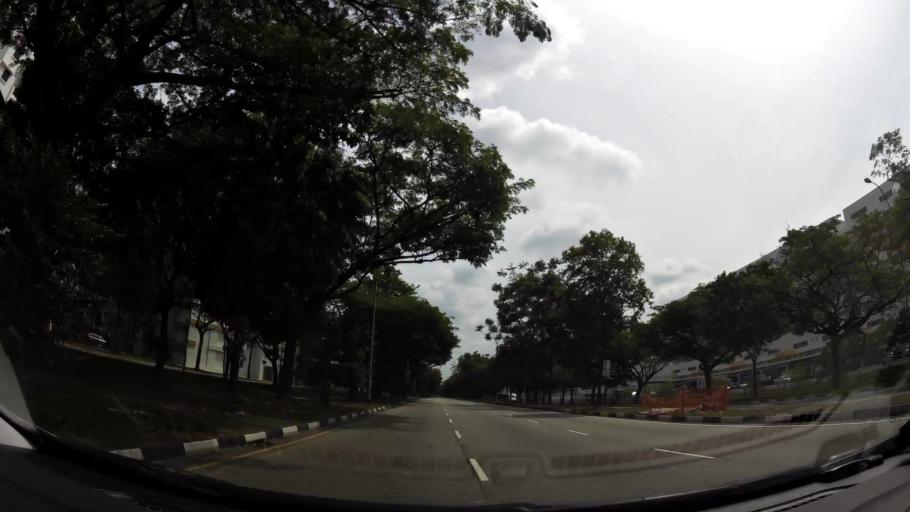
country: MY
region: Johor
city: Johor Bahru
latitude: 1.3349
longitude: 103.6995
